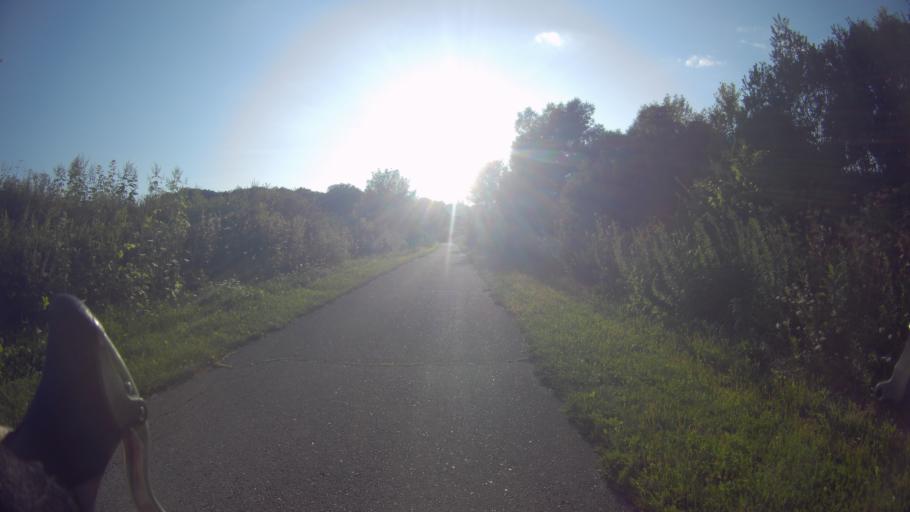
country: US
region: Wisconsin
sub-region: Dane County
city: Madison
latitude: 43.0103
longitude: -89.4195
